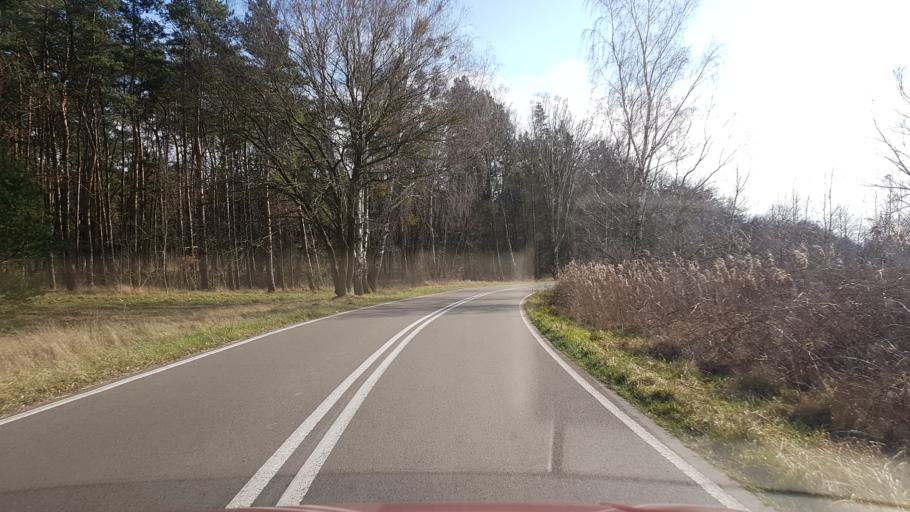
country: PL
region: West Pomeranian Voivodeship
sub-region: Powiat policki
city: Nowe Warpno
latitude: 53.7282
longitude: 14.3120
